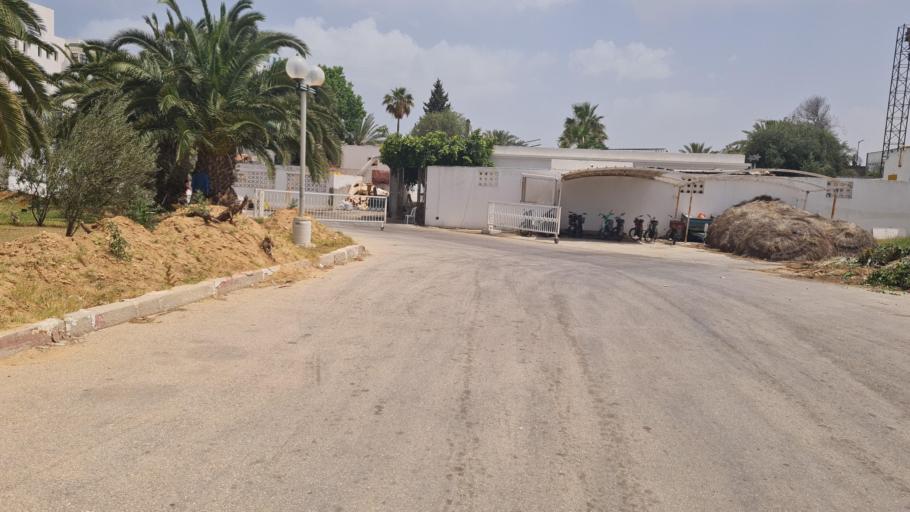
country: TN
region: Susah
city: Port el Kantaoui
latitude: 35.9026
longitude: 10.5837
